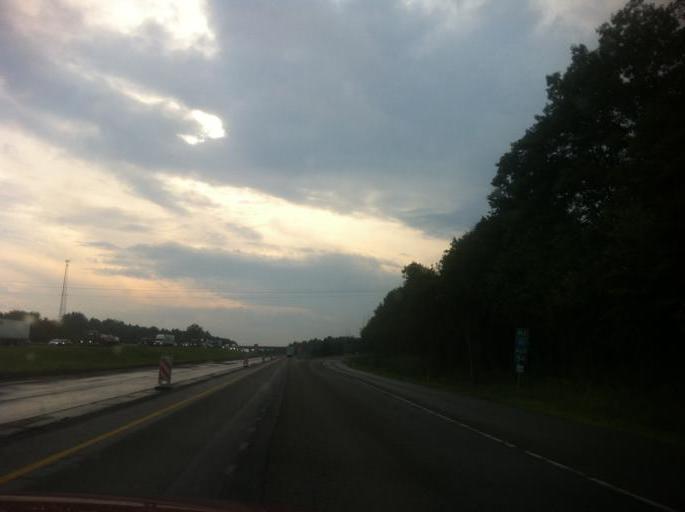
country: US
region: Pennsylvania
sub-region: Clarion County
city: Knox
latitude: 41.1837
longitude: -79.5341
